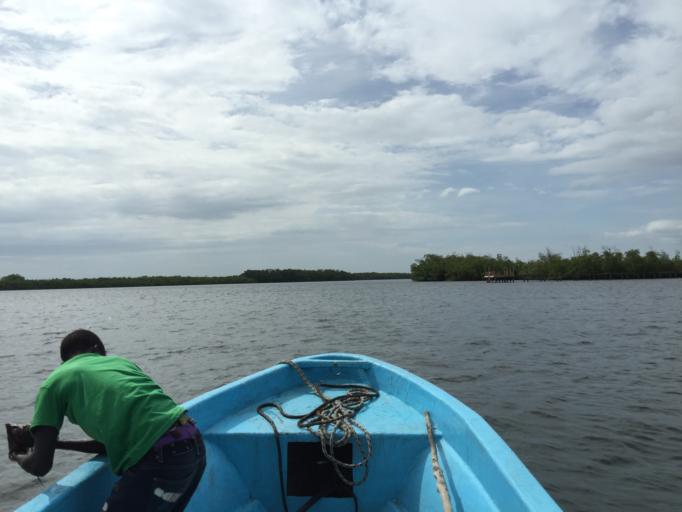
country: SN
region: Fatick
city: Sokone
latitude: 13.7957
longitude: -16.4807
